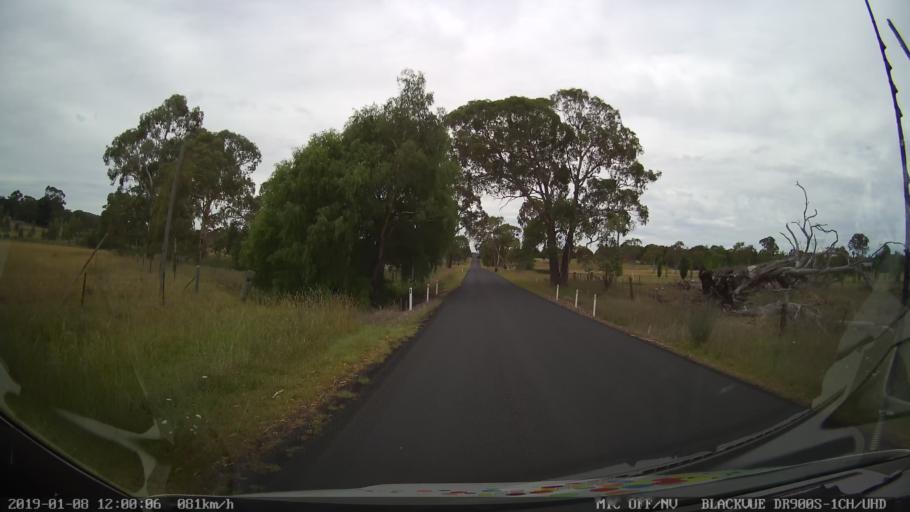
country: AU
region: New South Wales
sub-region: Armidale Dumaresq
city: Armidale
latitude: -30.4598
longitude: 151.5969
